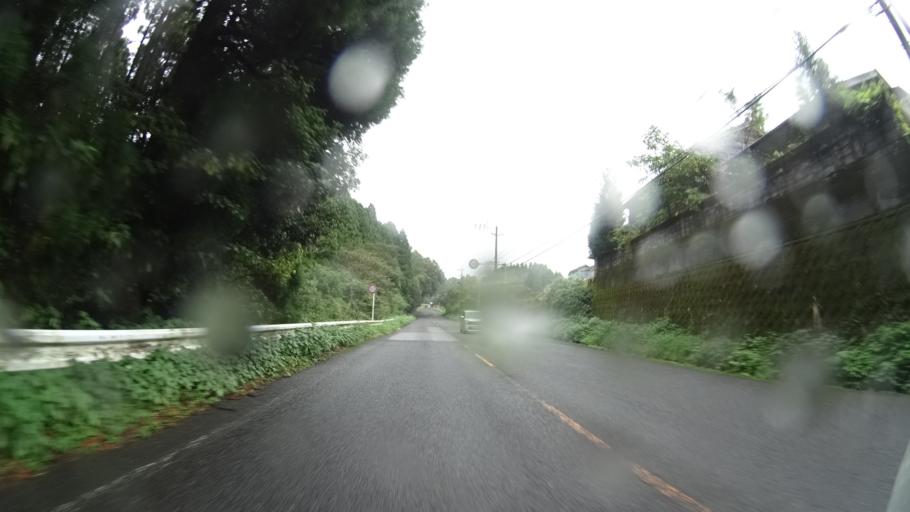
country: JP
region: Kagoshima
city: Kajiki
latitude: 31.7888
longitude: 130.6760
